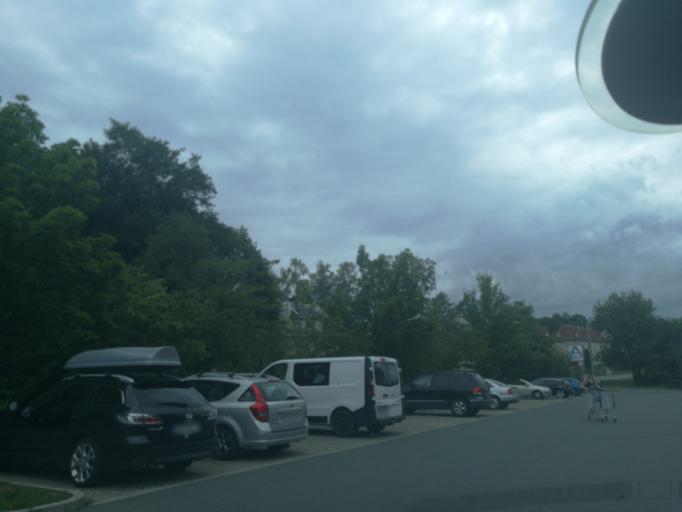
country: DE
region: Saxony
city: Adorf
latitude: 50.3080
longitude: 12.2532
